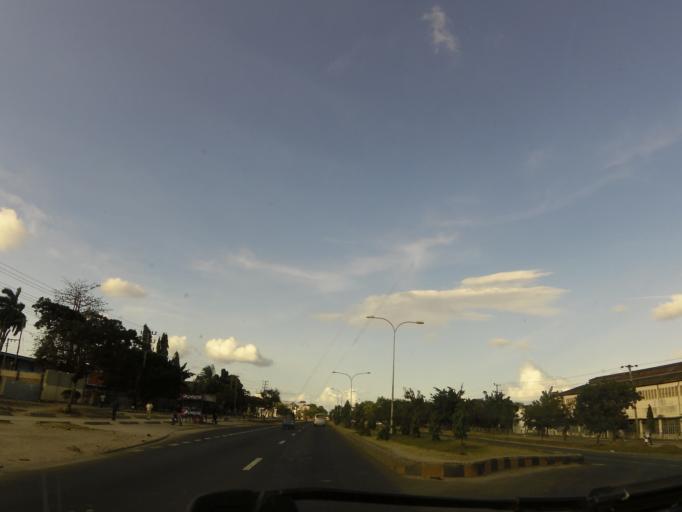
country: TZ
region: Dar es Salaam
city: Dar es Salaam
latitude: -6.8482
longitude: 39.2365
